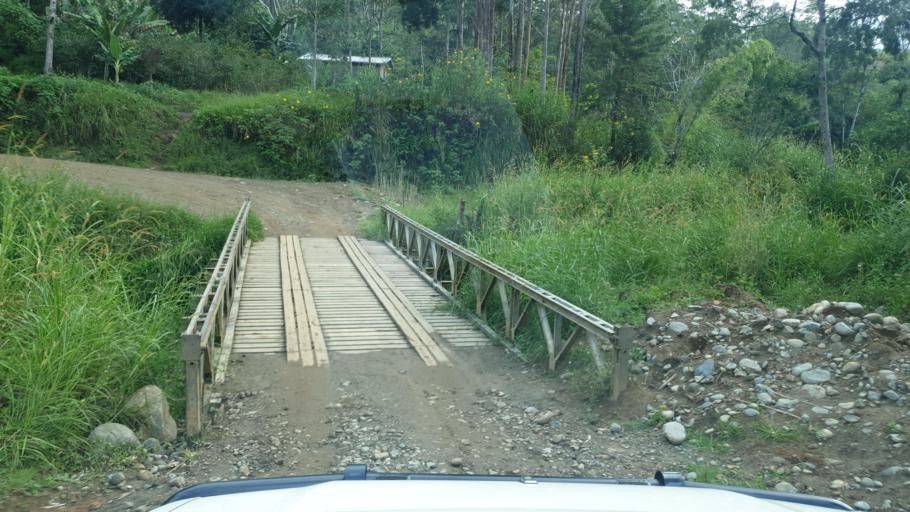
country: PG
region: Eastern Highlands
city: Goroka
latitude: -5.9406
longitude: 145.2697
